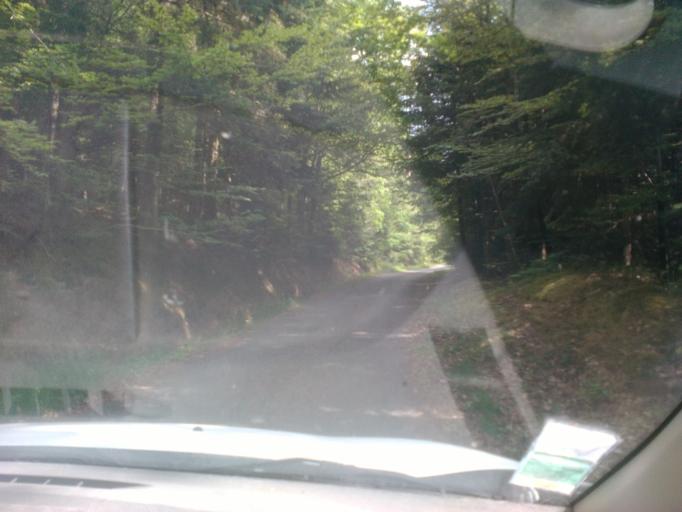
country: FR
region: Lorraine
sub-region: Departement des Vosges
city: Moyenmoutier
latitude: 48.3893
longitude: 6.9359
